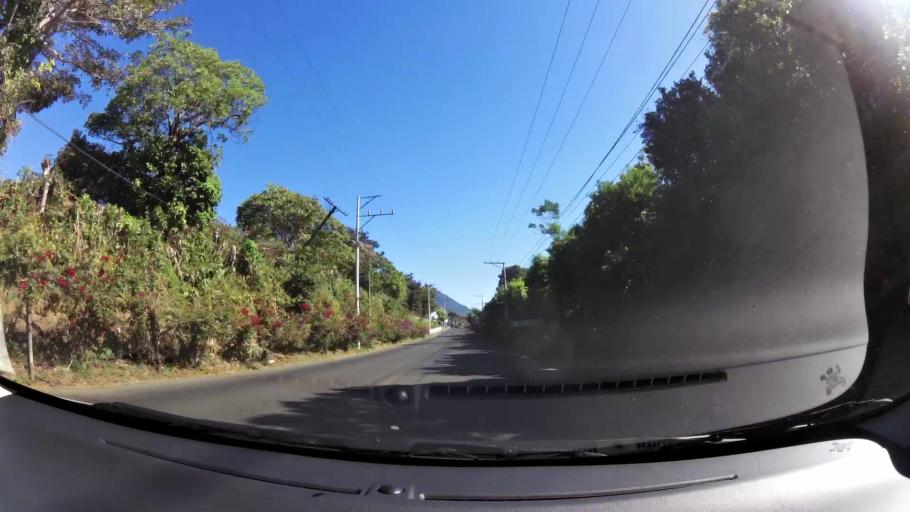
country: SV
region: Sonsonate
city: Juayua
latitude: 13.8412
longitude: -89.7510
